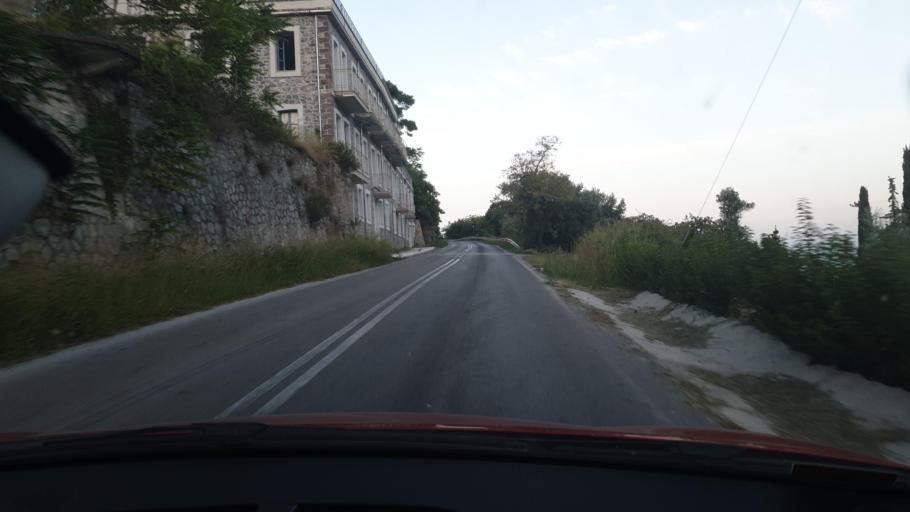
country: GR
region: Central Greece
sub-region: Nomos Evvoias
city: Kymi
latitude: 38.6333
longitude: 24.1098
